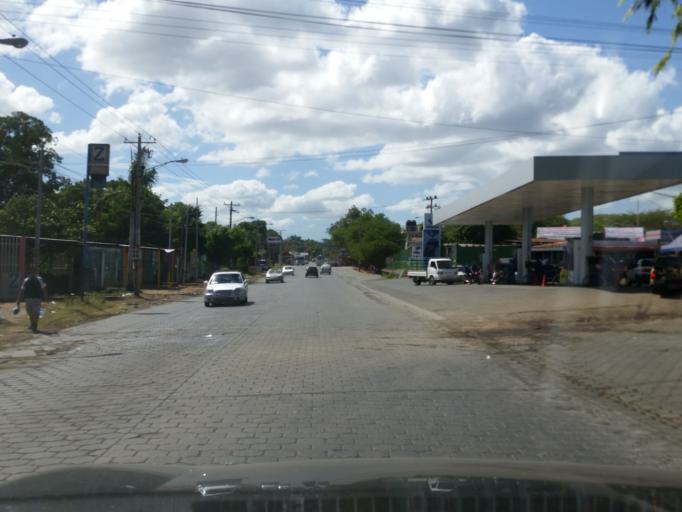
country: NI
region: Managua
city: Managua
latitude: 12.1287
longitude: -86.2026
